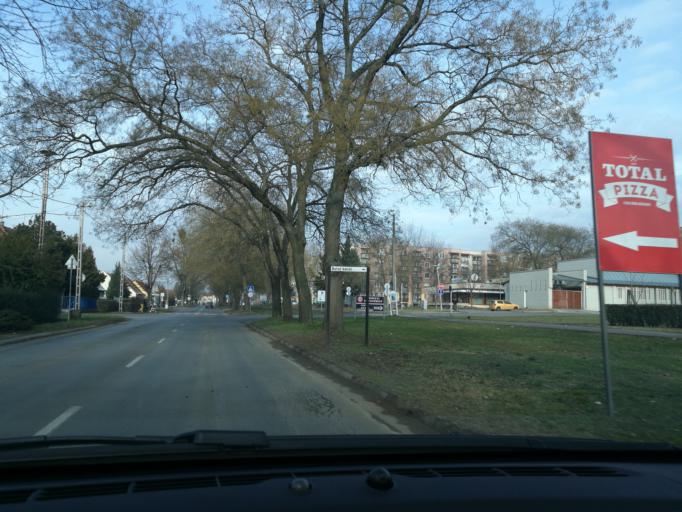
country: HU
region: Szabolcs-Szatmar-Bereg
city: Nyiregyhaza
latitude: 47.9585
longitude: 21.7356
